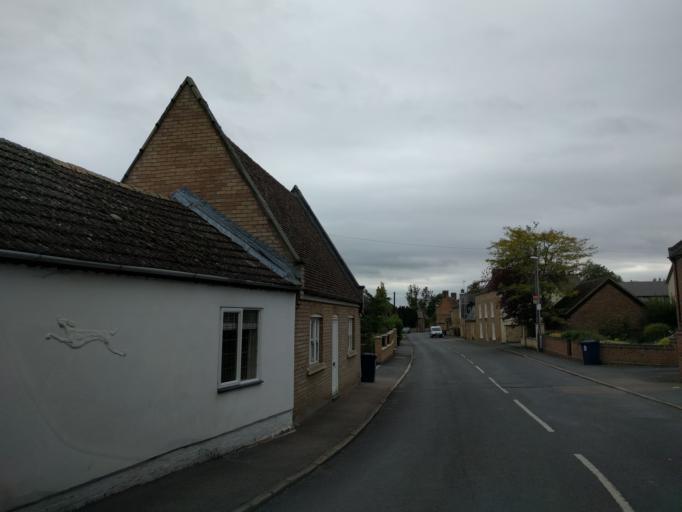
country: GB
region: England
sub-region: Cambridgeshire
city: Earith
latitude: 52.3539
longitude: 0.0068
